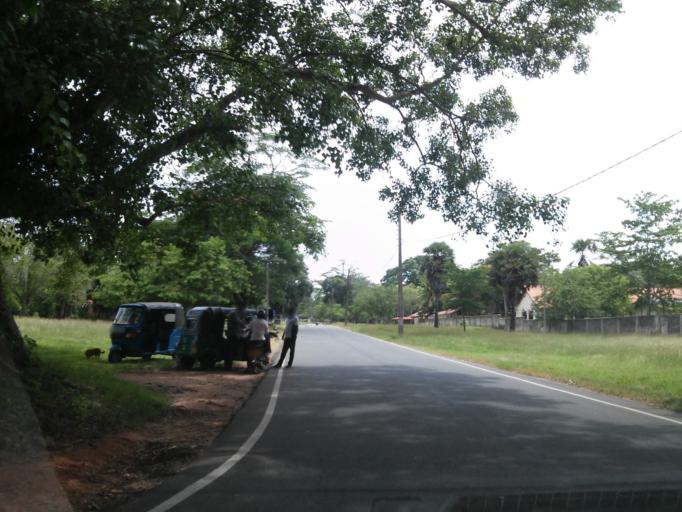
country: LK
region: North Central
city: Anuradhapura
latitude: 8.3477
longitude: 80.4020
